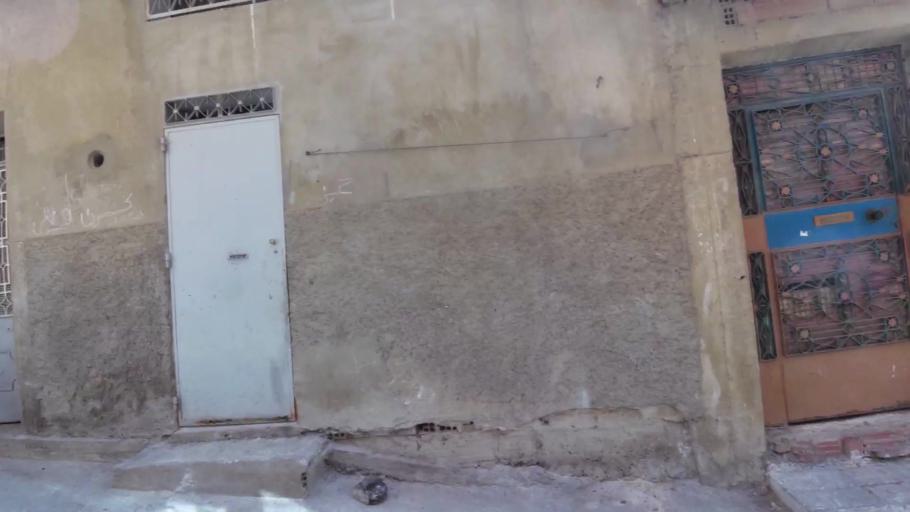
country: MA
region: Tanger-Tetouan
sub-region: Tanger-Assilah
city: Tangier
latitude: 35.7410
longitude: -5.8024
